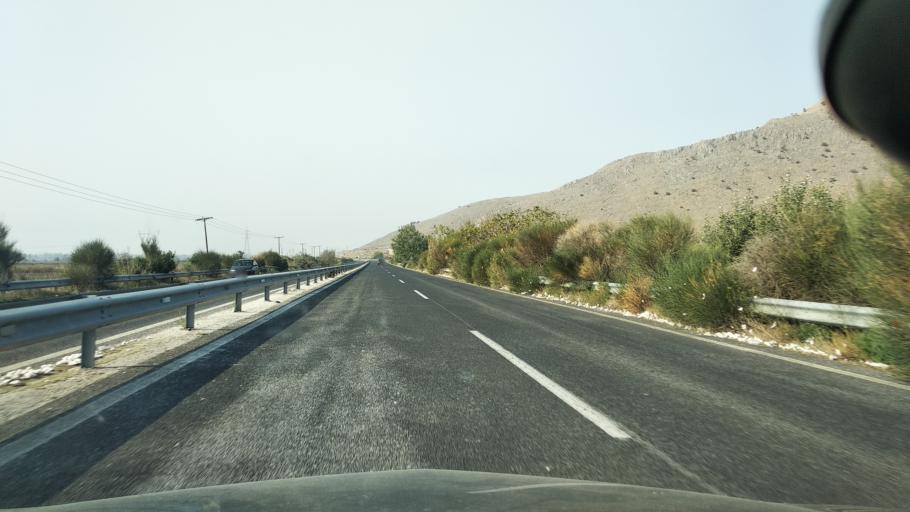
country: GR
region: Thessaly
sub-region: Trikala
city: Farkadona
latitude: 39.5921
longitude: 22.0915
